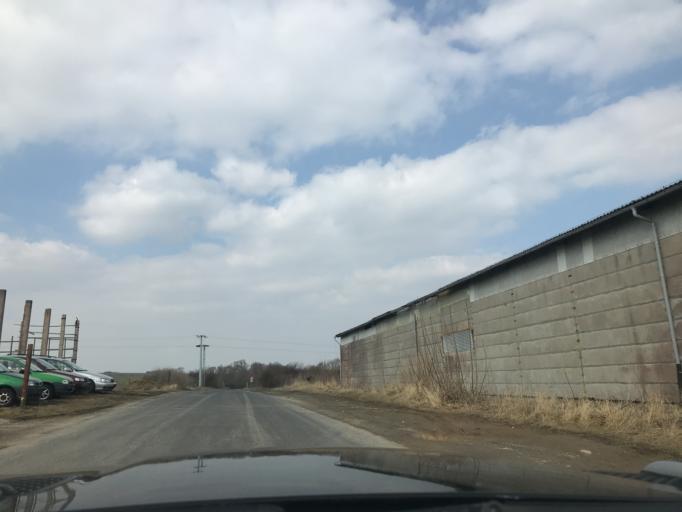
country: DE
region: Thuringia
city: Oberdorla
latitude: 51.2145
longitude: 10.3992
